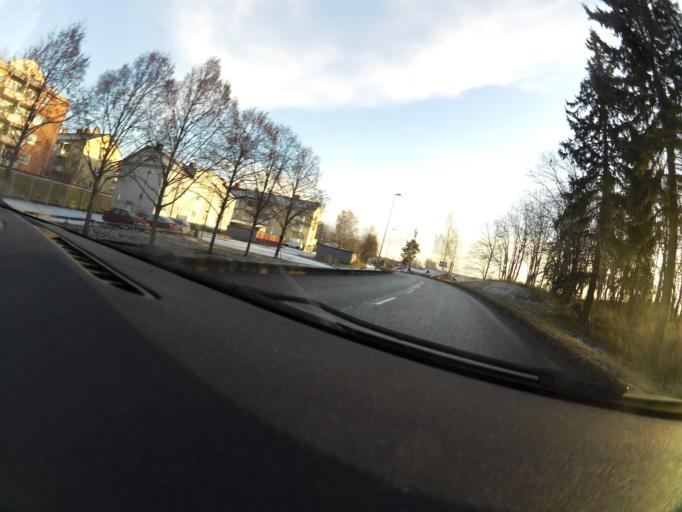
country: SE
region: Gaevleborg
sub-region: Gavle Kommun
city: Gavle
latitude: 60.6679
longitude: 17.1617
